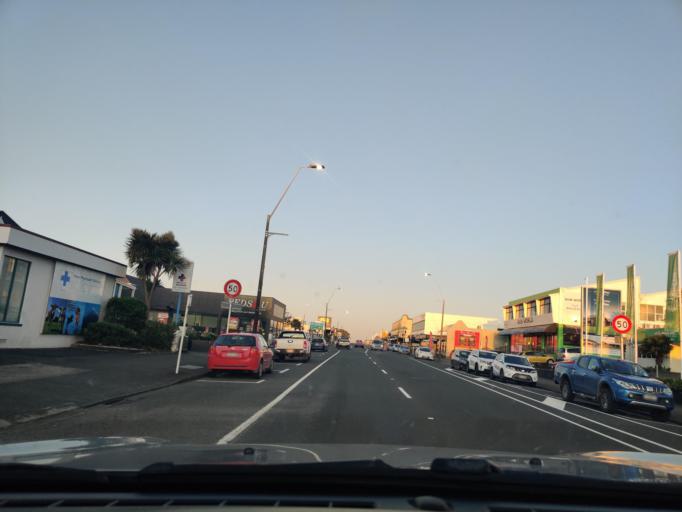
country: NZ
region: Taranaki
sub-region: New Plymouth District
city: New Plymouth
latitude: -39.0556
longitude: 174.0812
